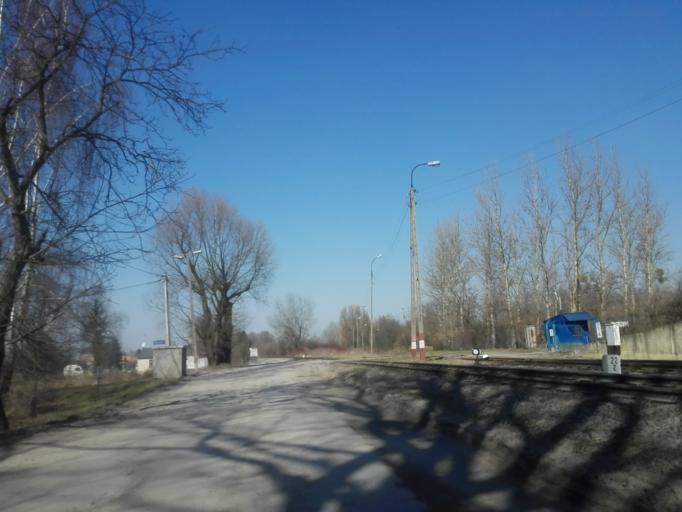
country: PL
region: Masovian Voivodeship
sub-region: Warszawa
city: Wilanow
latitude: 52.1519
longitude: 21.1403
